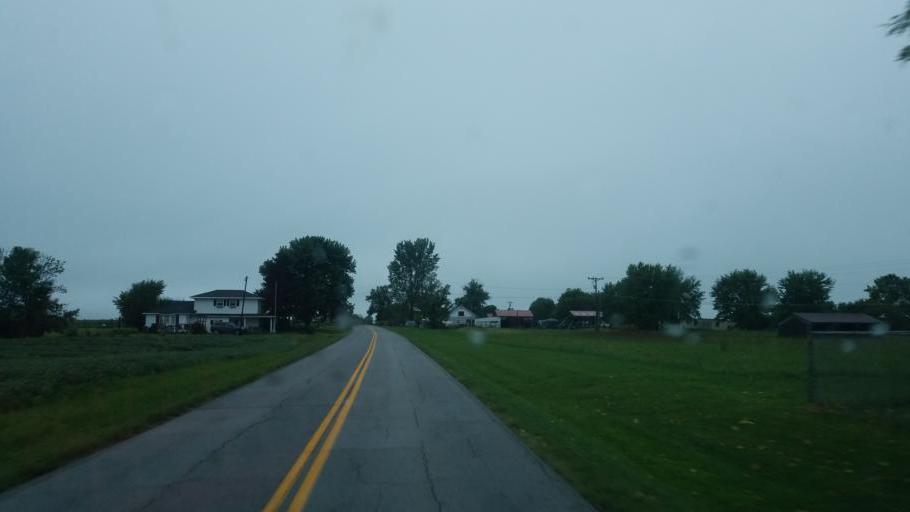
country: US
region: Kentucky
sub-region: Fleming County
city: Flemingsburg
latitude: 38.4124
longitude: -83.6597
